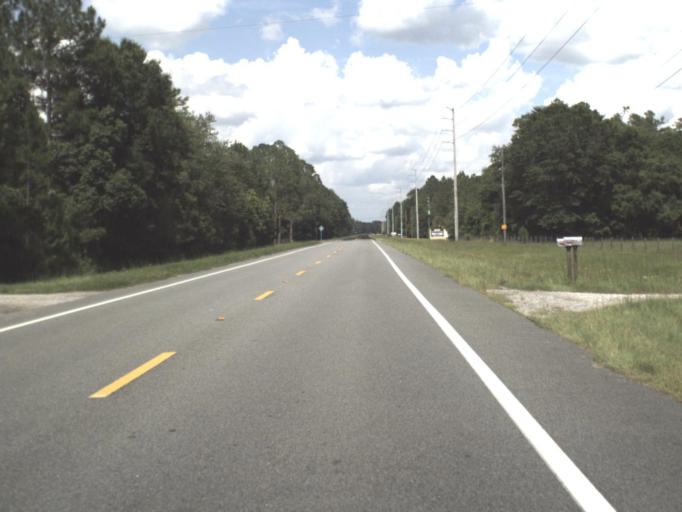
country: US
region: Florida
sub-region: Bradford County
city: Starke
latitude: 29.9506
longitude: -82.0881
